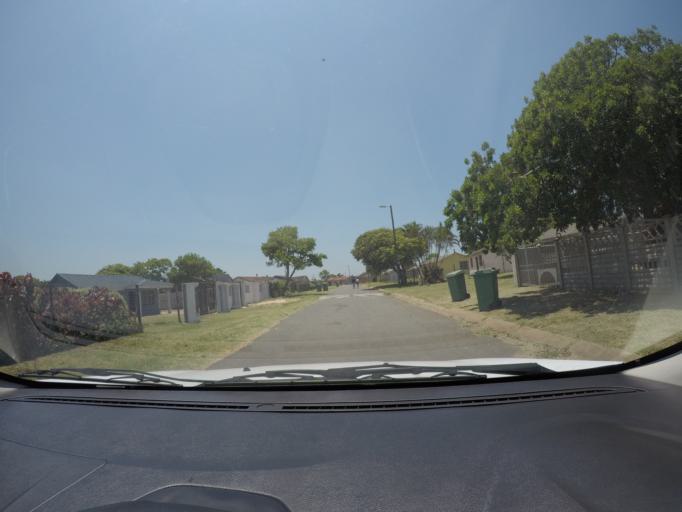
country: ZA
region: KwaZulu-Natal
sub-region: uThungulu District Municipality
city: eSikhawini
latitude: -28.8834
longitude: 31.9005
